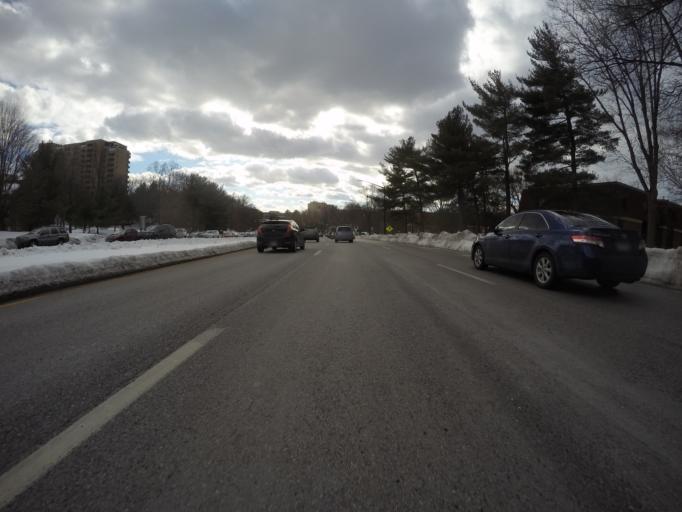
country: US
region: Maryland
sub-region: Howard County
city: Columbia
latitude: 39.2255
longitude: -76.8558
